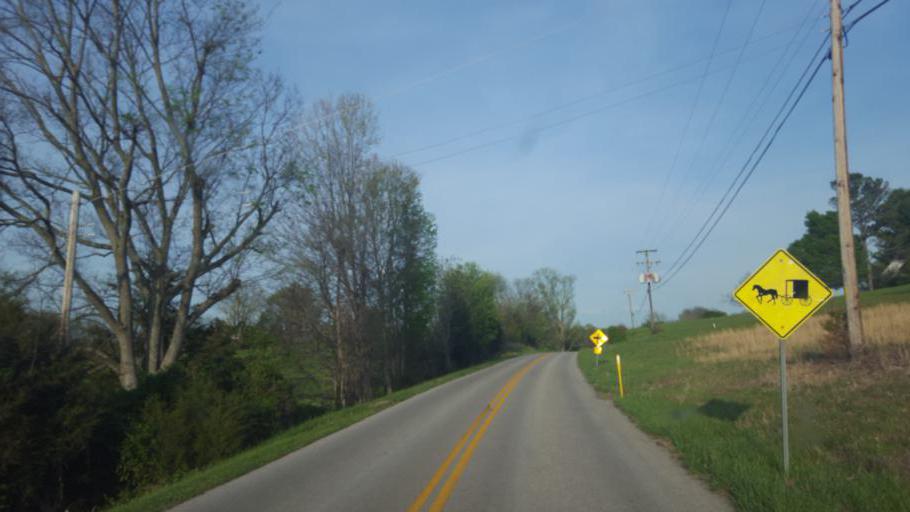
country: US
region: Kentucky
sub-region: Barren County
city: Glasgow
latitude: 36.9385
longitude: -86.0748
